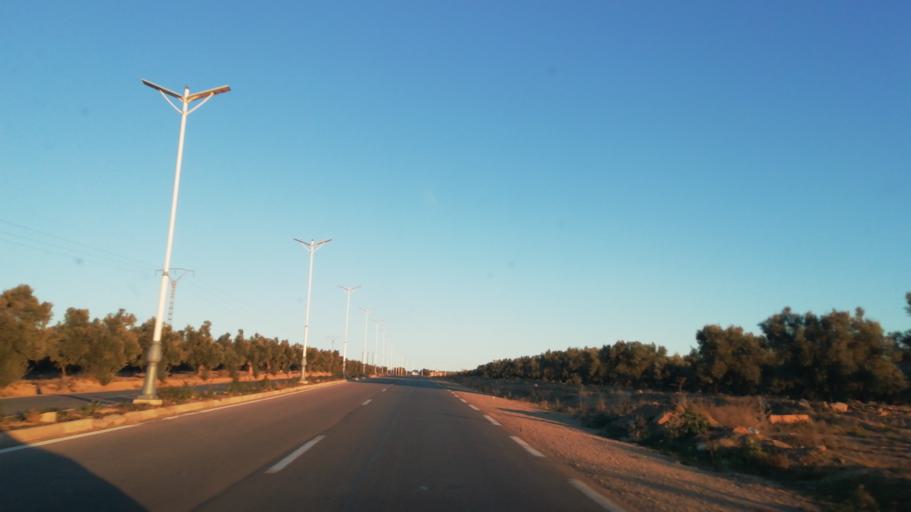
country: DZ
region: Saida
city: Saida
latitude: 34.8651
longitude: 0.1881
